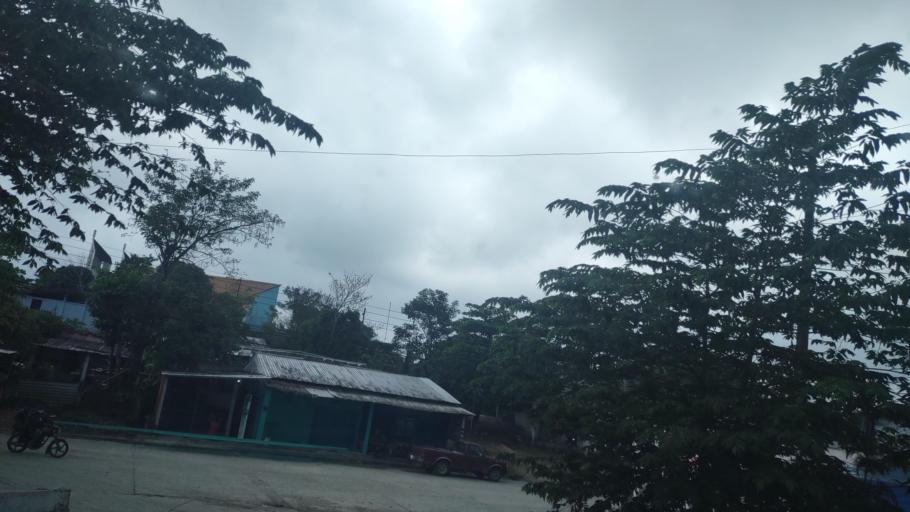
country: MX
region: Veracruz
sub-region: Uxpanapa
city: Poblado 10
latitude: 17.4951
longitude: -94.1634
